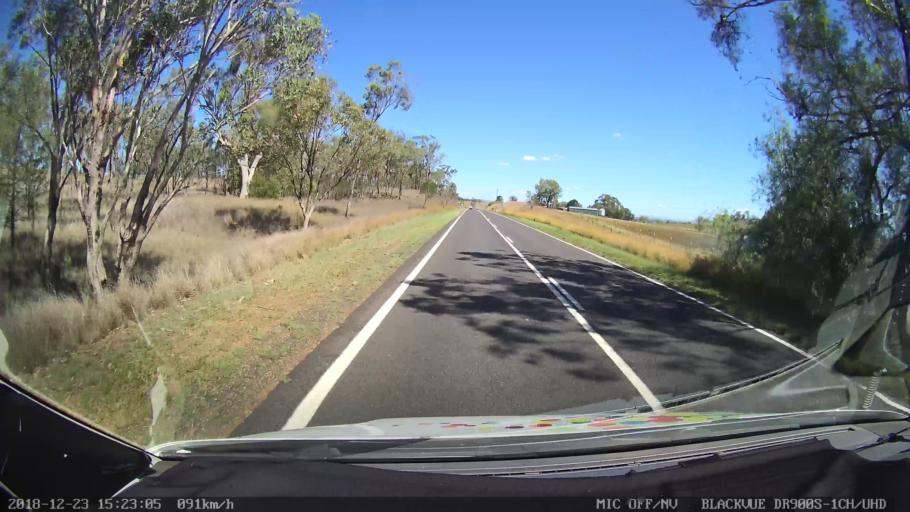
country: AU
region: New South Wales
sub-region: Tamworth Municipality
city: Manilla
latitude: -30.8761
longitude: 150.8108
